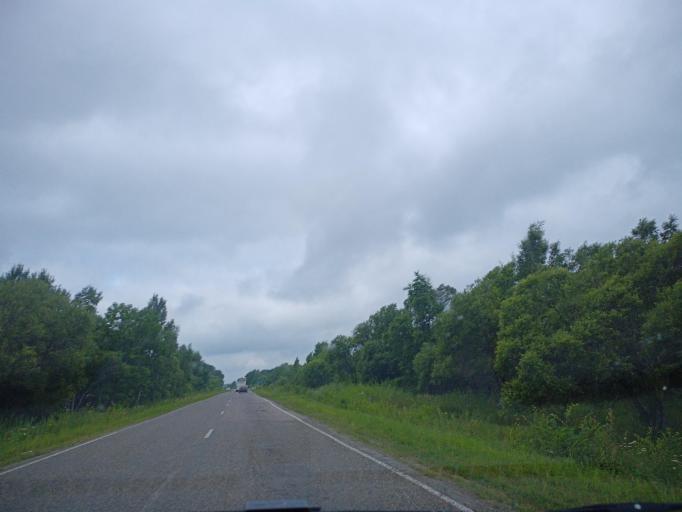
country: RU
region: Primorskiy
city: Novopokrovka
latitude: 45.9706
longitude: 134.2376
